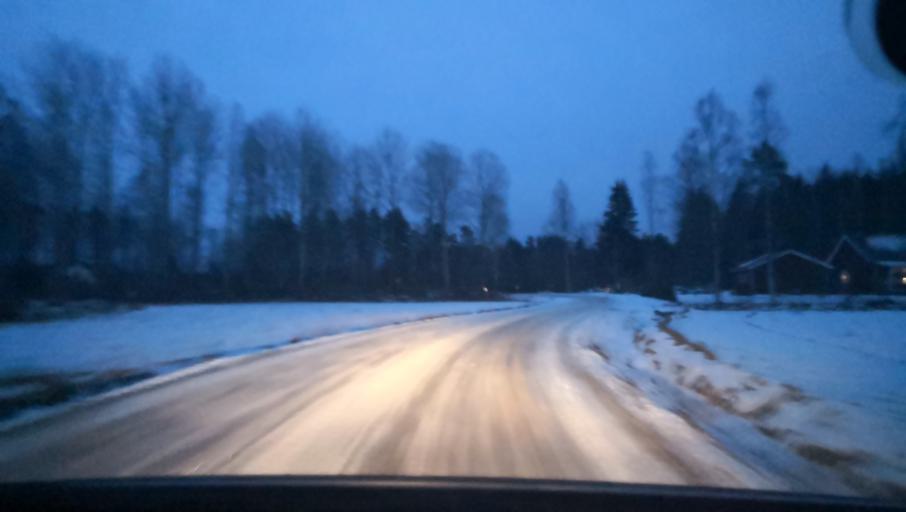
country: SE
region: Uppsala
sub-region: Heby Kommun
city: Tarnsjo
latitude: 60.2431
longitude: 16.6912
